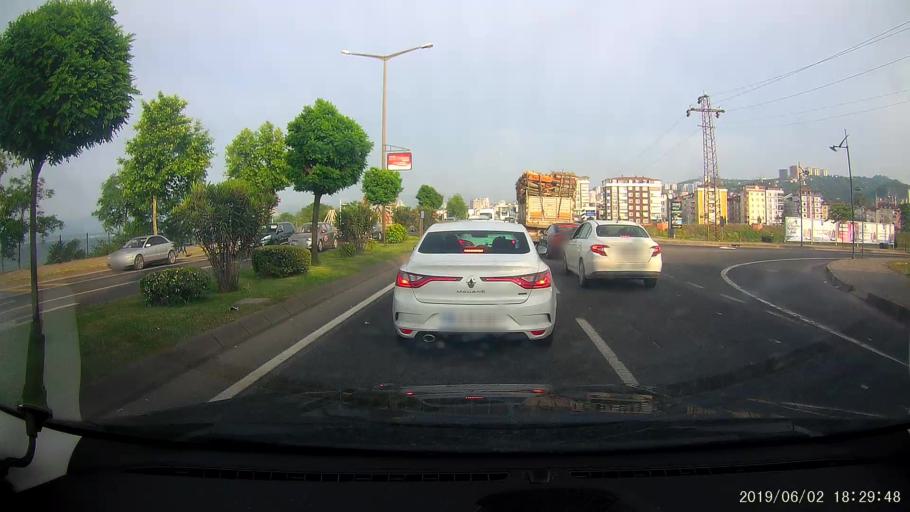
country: TR
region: Ordu
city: Fatsa
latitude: 41.0382
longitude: 37.4912
